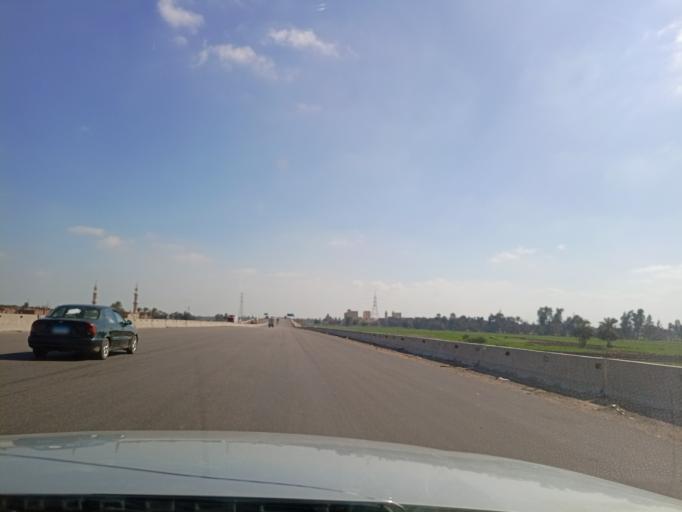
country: EG
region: Eastern Province
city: Mashtul as Suq
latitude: 30.4620
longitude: 31.3253
